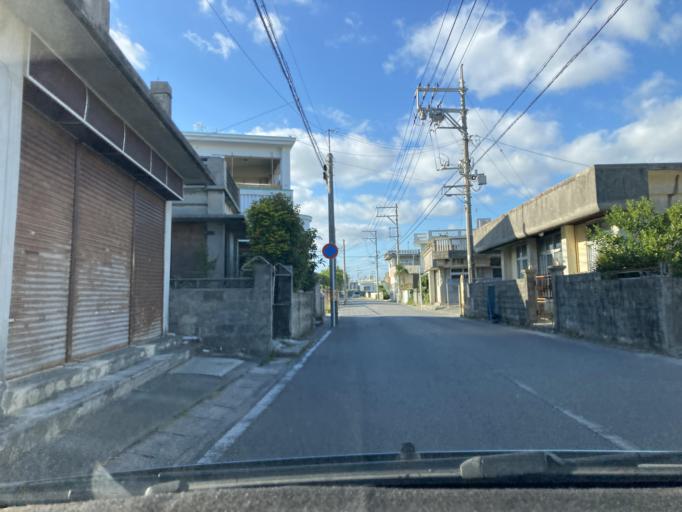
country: JP
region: Okinawa
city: Katsuren-haebaru
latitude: 26.3250
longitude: 127.9048
